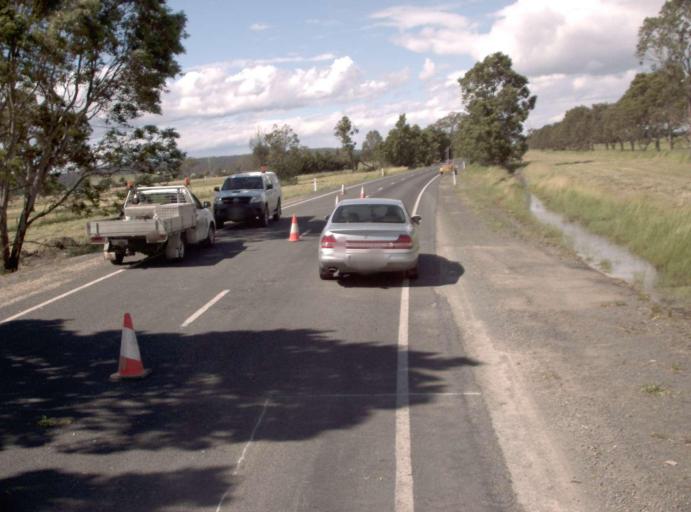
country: AU
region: Victoria
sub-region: Latrobe
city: Traralgon
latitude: -38.1461
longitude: 146.5242
